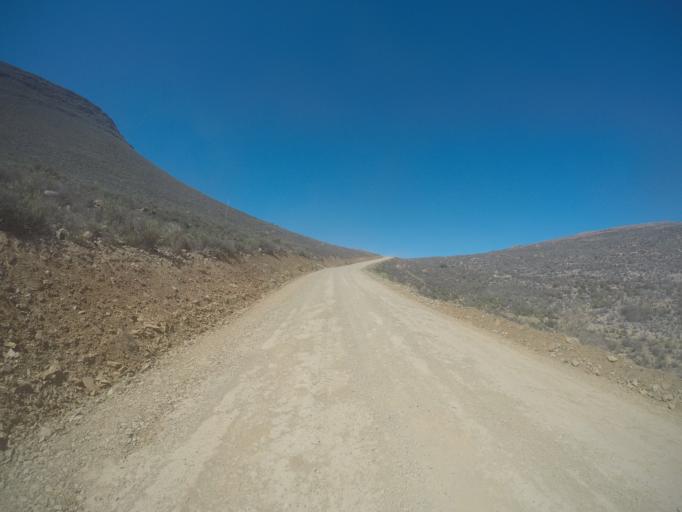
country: ZA
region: Western Cape
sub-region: West Coast District Municipality
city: Clanwilliam
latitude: -32.6072
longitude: 19.3677
